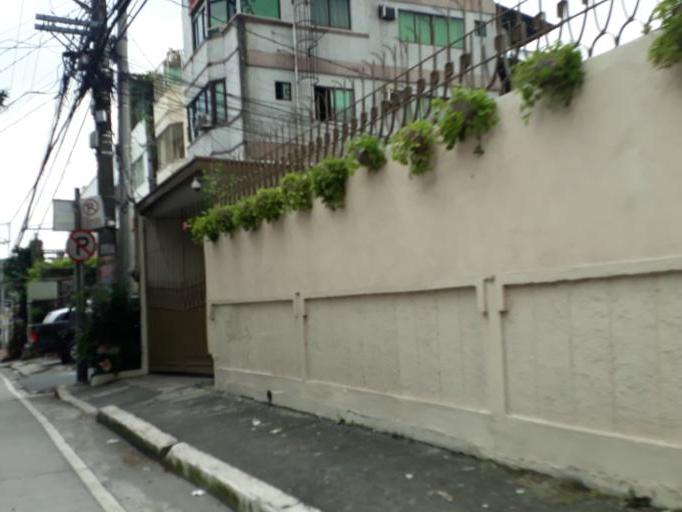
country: PH
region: Calabarzon
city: Bagong Pagasa
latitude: 14.6598
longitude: 121.0424
